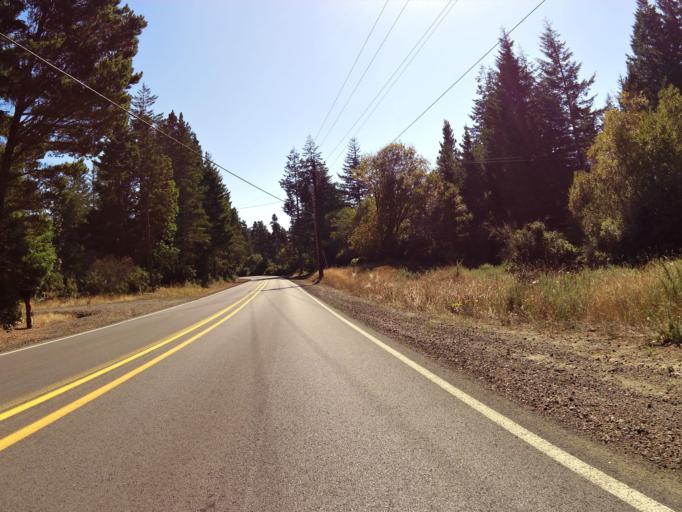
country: US
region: Oregon
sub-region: Coos County
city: Bandon
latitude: 43.2098
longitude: -124.3695
